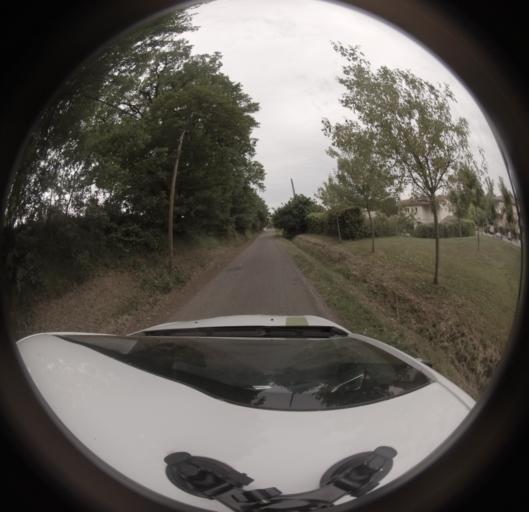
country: FR
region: Midi-Pyrenees
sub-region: Departement du Tarn-et-Garonne
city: Montauban
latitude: 44.0104
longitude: 1.3925
